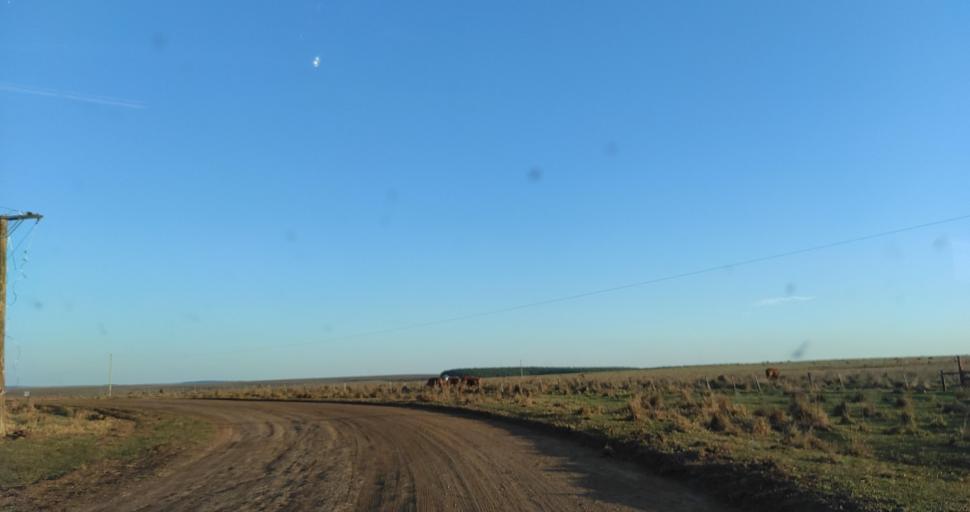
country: PY
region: Itapua
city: San Juan del Parana
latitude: -27.4336
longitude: -56.0851
